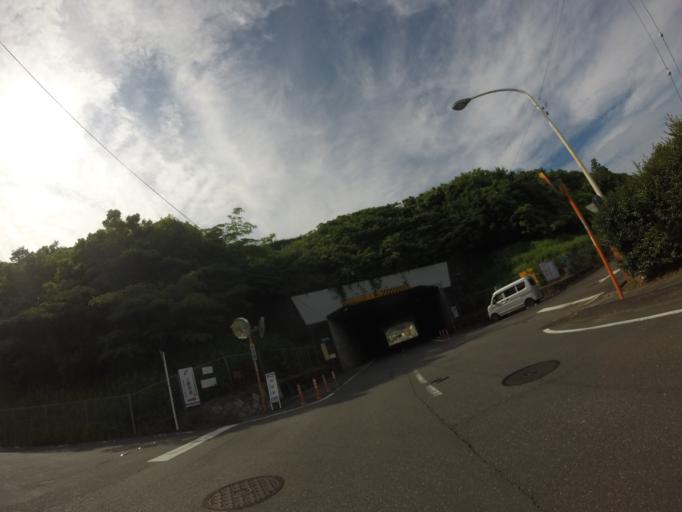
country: JP
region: Shizuoka
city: Shimada
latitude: 34.7589
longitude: 138.2020
